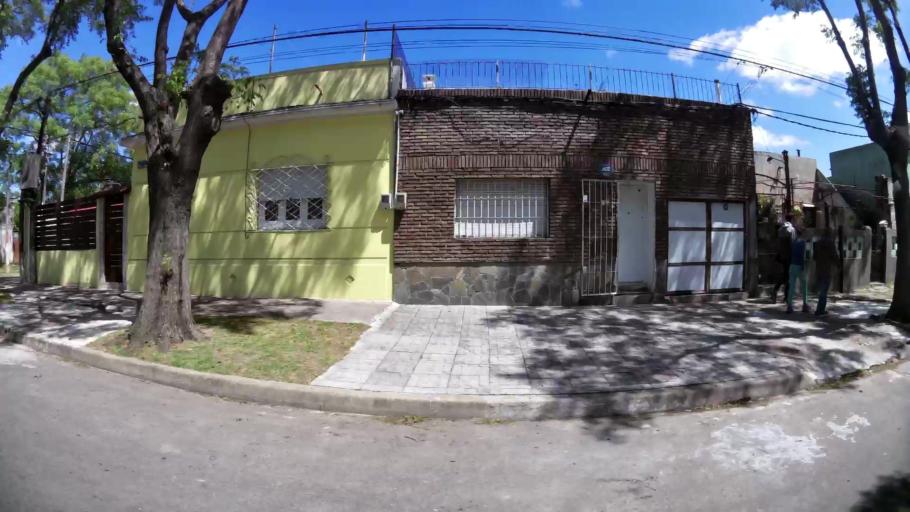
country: UY
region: Montevideo
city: Montevideo
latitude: -34.8610
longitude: -56.1317
